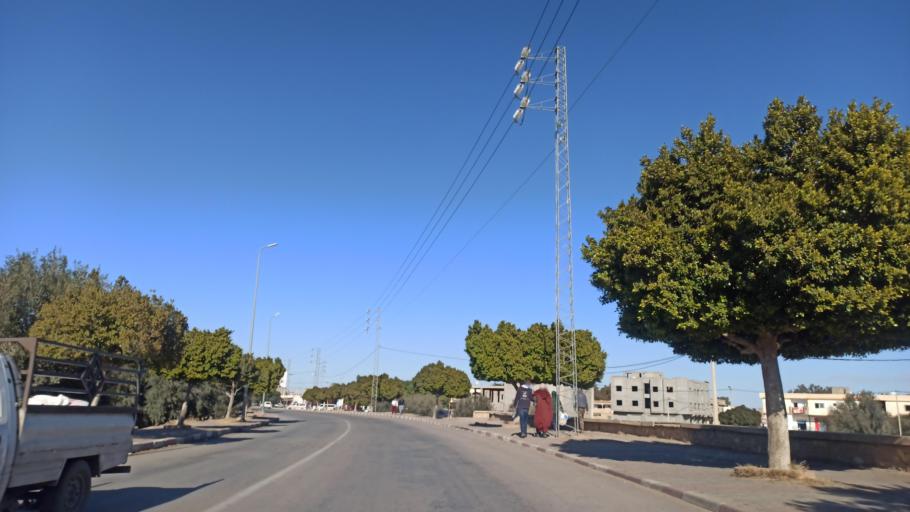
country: TN
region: Sidi Bu Zayd
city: Jilma
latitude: 35.2704
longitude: 9.4189
